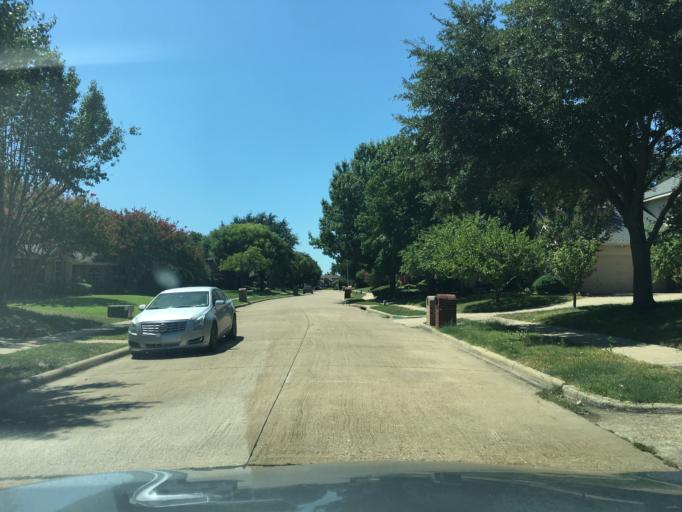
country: US
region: Texas
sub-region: Dallas County
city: Sachse
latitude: 32.9648
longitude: -96.6316
